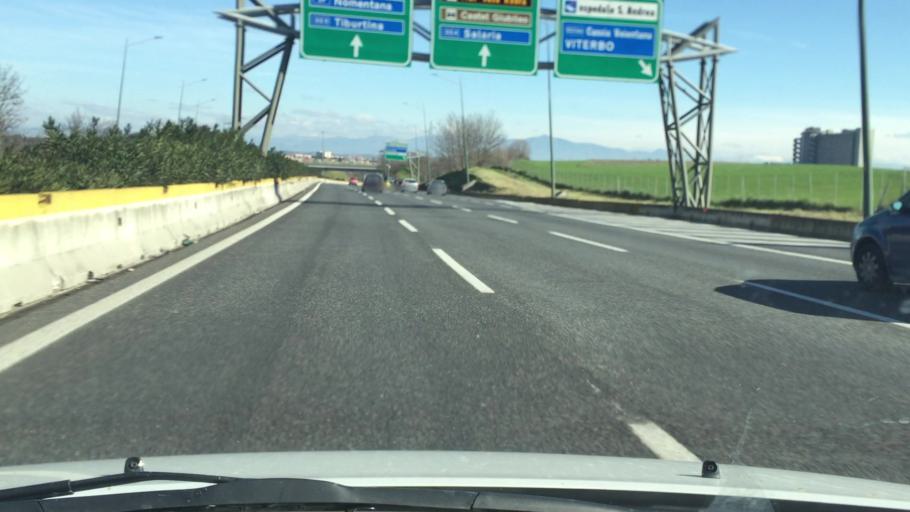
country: VA
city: Vatican City
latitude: 41.9825
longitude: 12.4612
